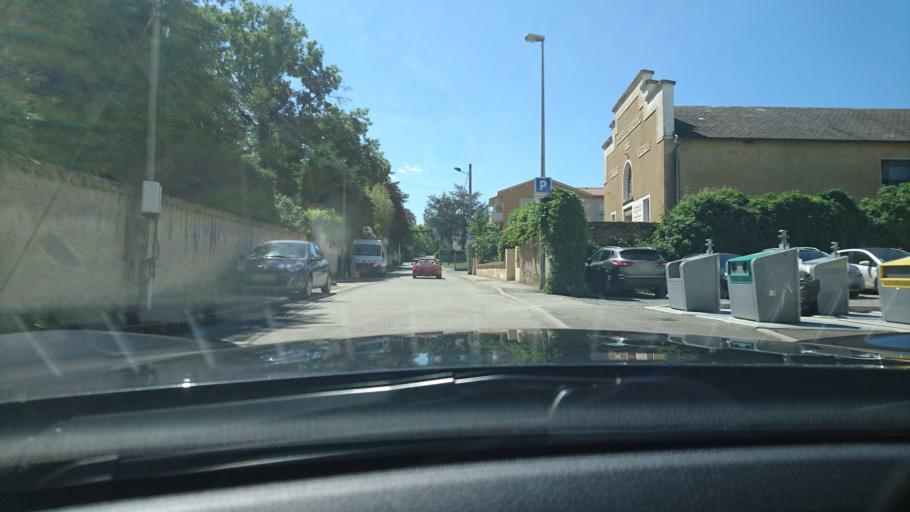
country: FR
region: Rhone-Alpes
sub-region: Departement du Rhone
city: Grezieu-la-Varenne
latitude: 45.7474
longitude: 4.6886
